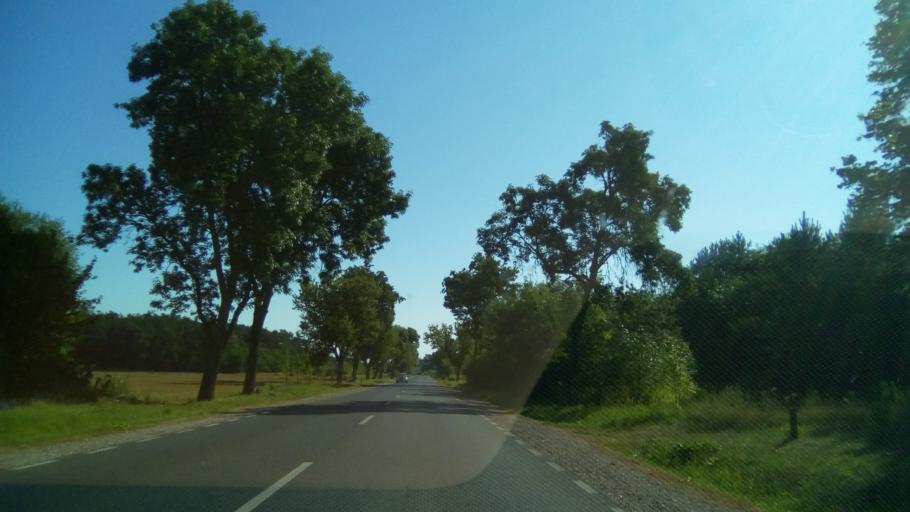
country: PL
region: Masovian Voivodeship
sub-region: Powiat plocki
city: Maszewo Duze
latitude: 52.5429
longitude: 19.6218
